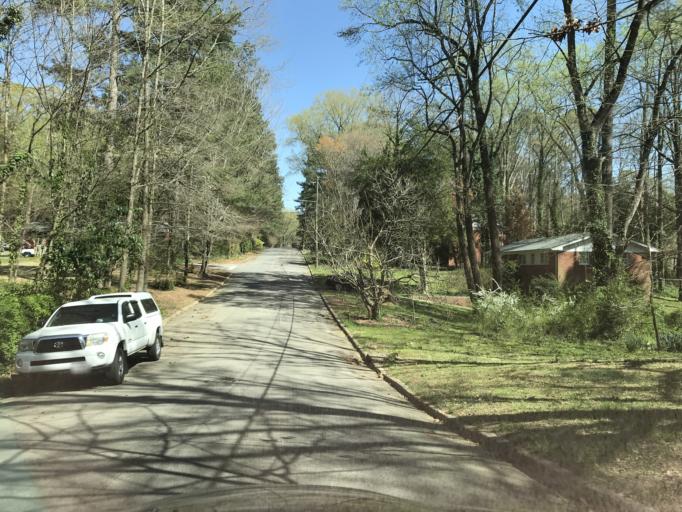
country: US
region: North Carolina
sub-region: Wake County
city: West Raleigh
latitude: 35.7721
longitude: -78.7059
